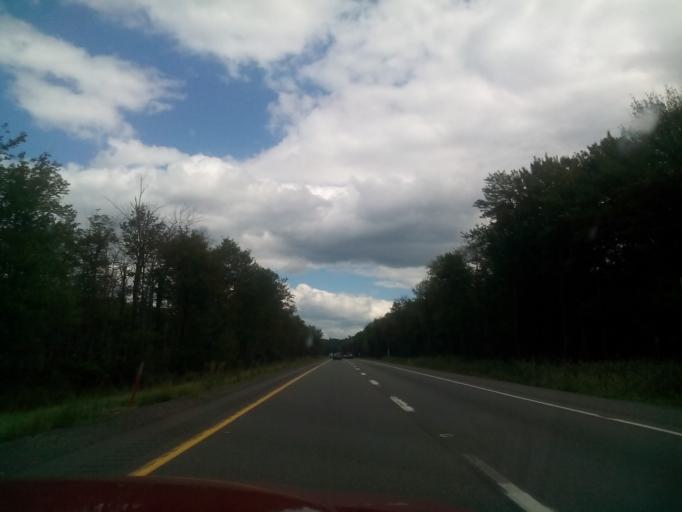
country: US
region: Pennsylvania
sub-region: Carbon County
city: Towamensing Trails
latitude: 41.0761
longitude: -75.5659
